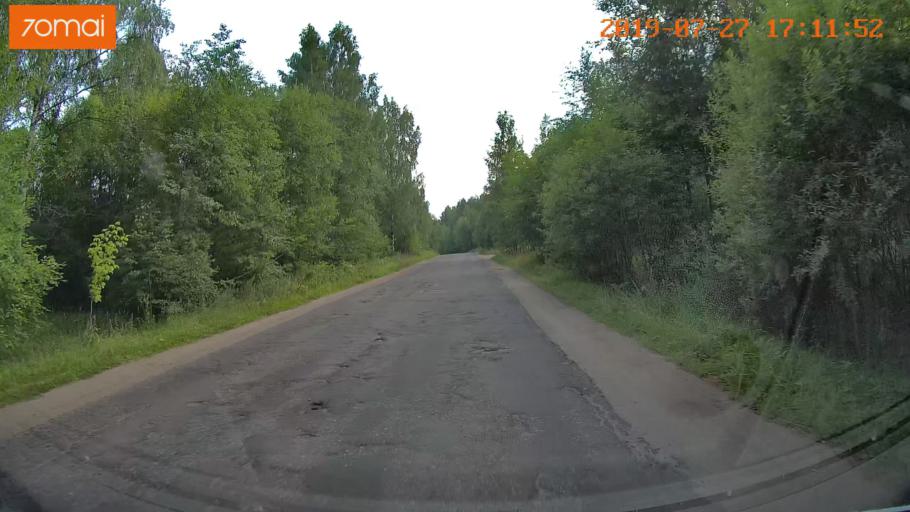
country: RU
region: Ivanovo
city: Novo-Talitsy
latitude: 57.0622
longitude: 40.8641
